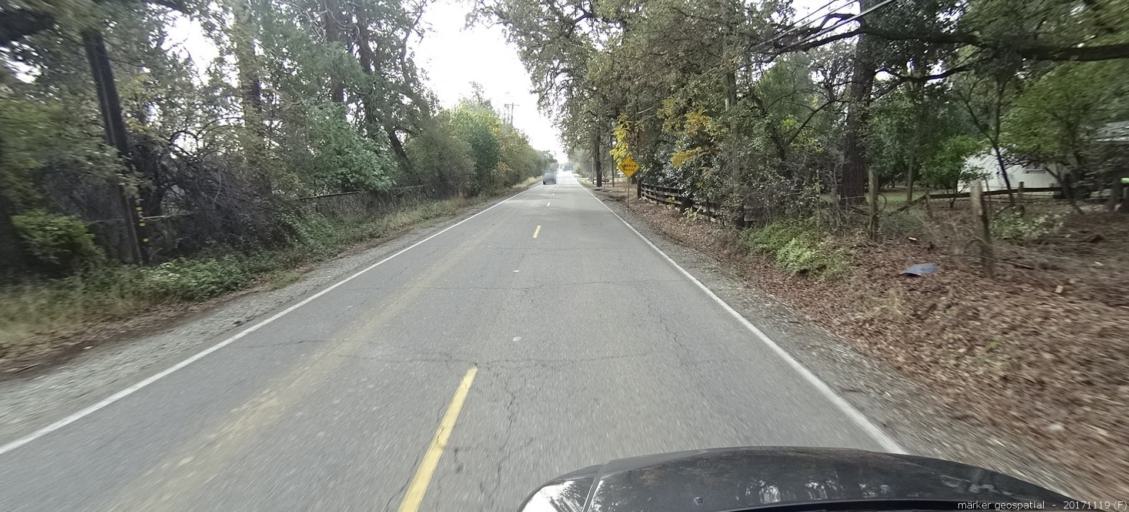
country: US
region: California
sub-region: Shasta County
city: Redding
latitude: 40.5251
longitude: -122.3337
